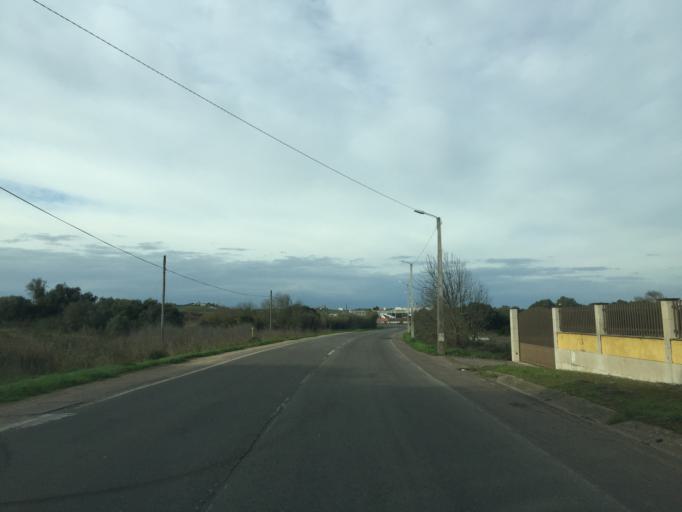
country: PT
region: Lisbon
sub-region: Sintra
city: Almargem
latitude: 38.8697
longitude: -9.2904
